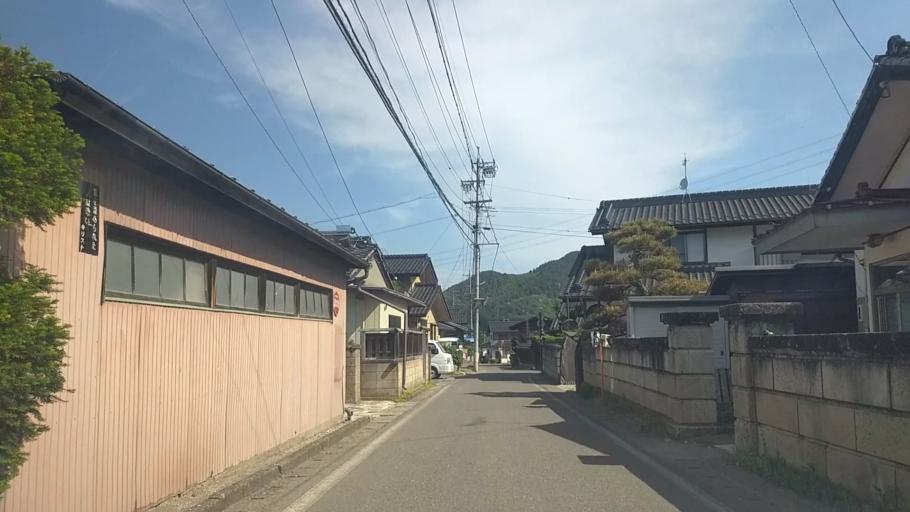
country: JP
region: Nagano
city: Saku
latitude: 36.1017
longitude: 138.4847
